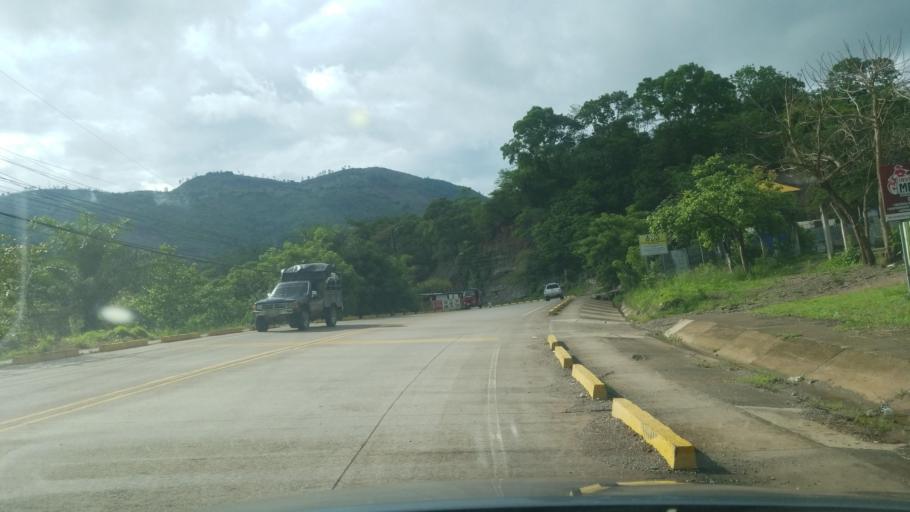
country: HN
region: Copan
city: Copan
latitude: 14.8395
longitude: -89.1623
